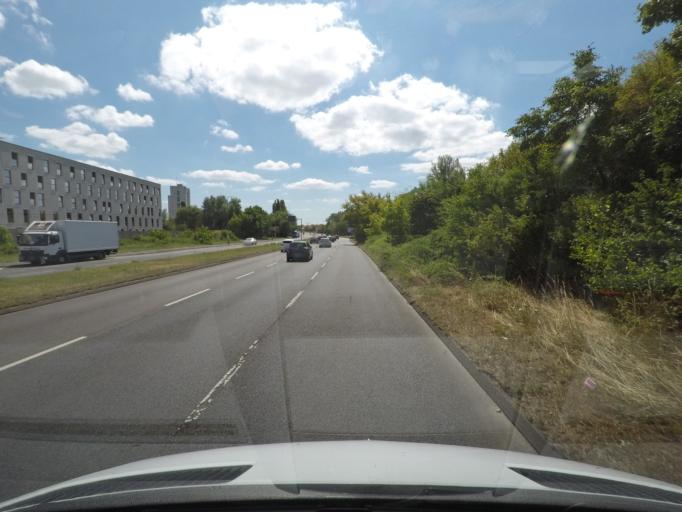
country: DE
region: Berlin
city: Falkenberg
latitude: 52.5387
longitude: 13.5386
